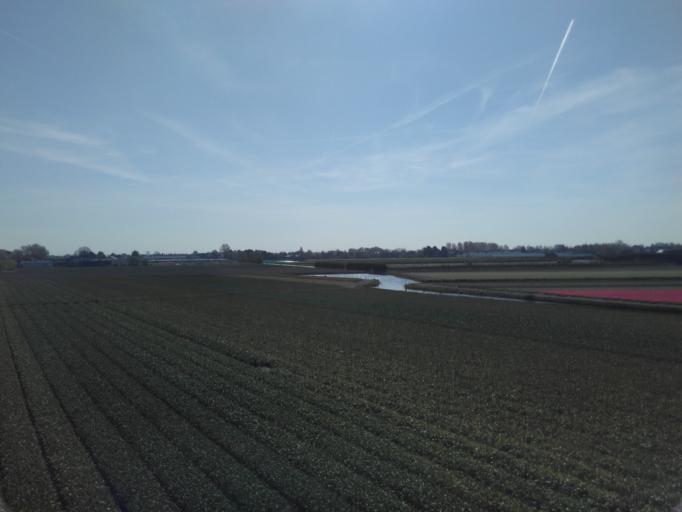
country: NL
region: North Holland
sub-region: Gemeente Bloemendaal
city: Bennebroek
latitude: 52.3131
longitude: 4.5770
